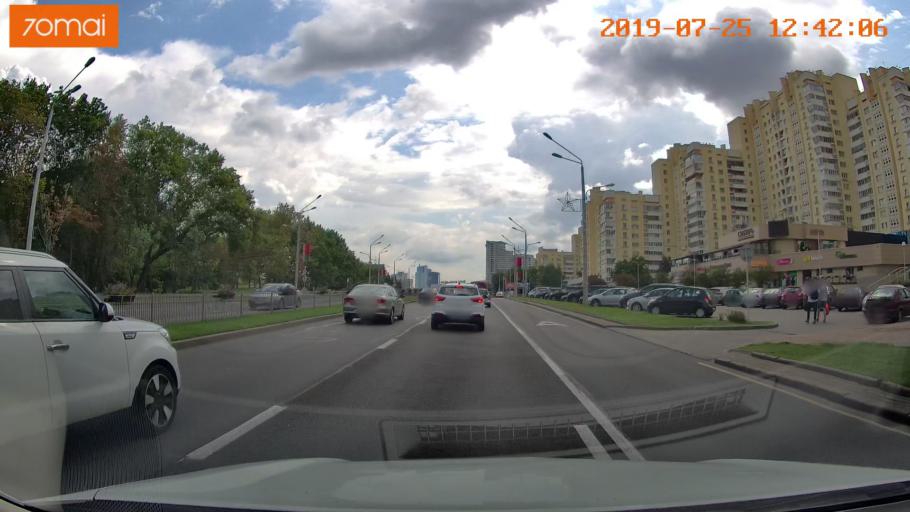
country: BY
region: Minsk
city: Minsk
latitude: 53.9181
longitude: 27.5329
